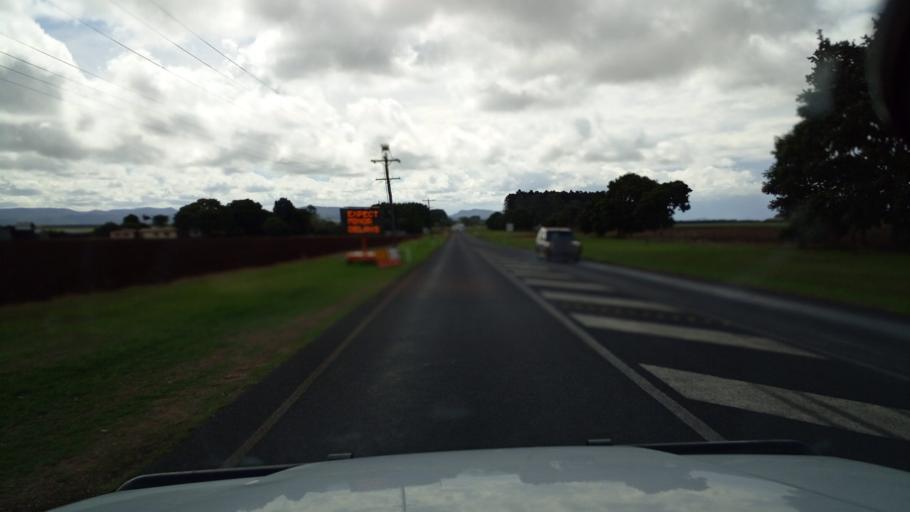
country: AU
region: Queensland
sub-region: Tablelands
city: Tolga
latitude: -17.2160
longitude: 145.5377
